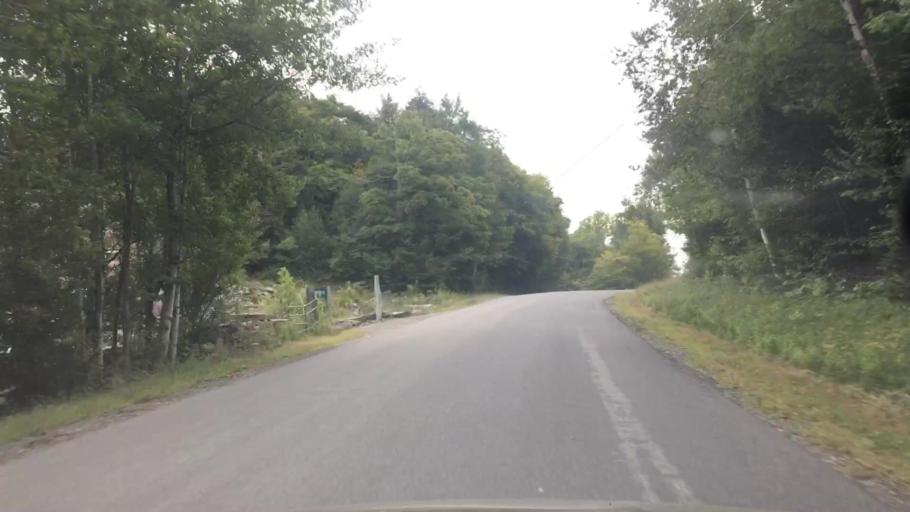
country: US
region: Vermont
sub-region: Windham County
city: Dover
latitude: 42.8400
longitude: -72.8226
